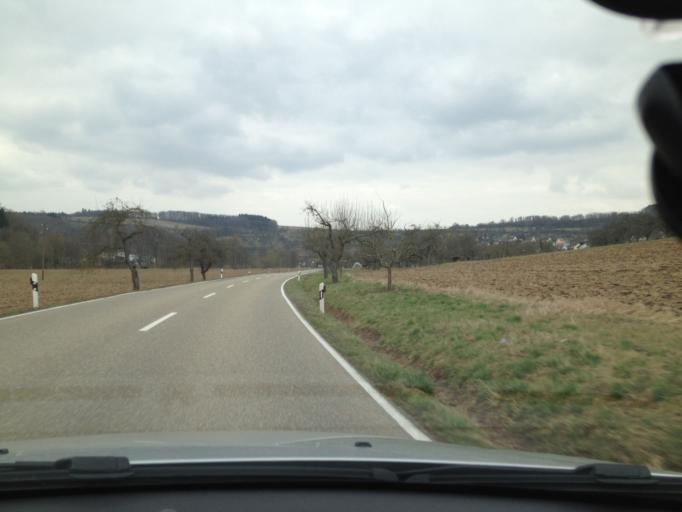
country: DE
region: Baden-Wuerttemberg
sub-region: Regierungsbezirk Stuttgart
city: Wertheim
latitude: 49.7212
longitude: 9.5280
